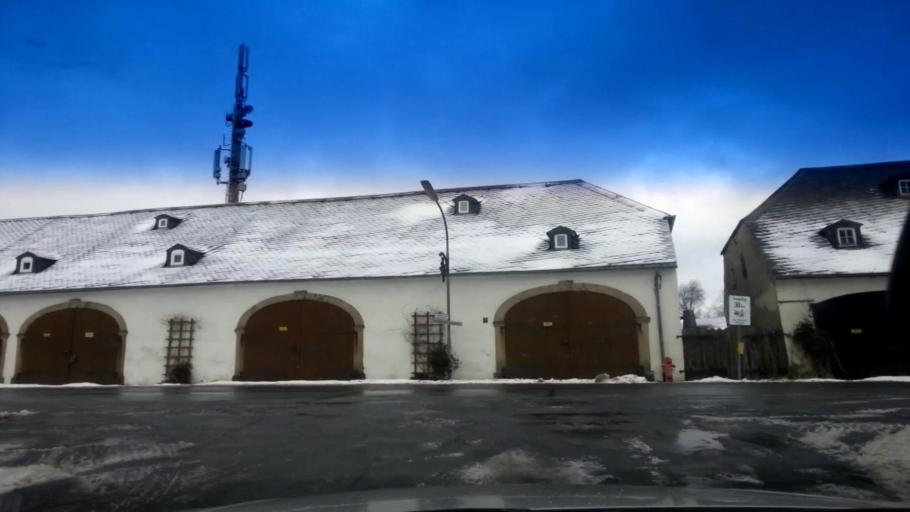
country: DE
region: Bavaria
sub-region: Upper Franconia
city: Weissenstadt
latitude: 50.1039
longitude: 11.8871
